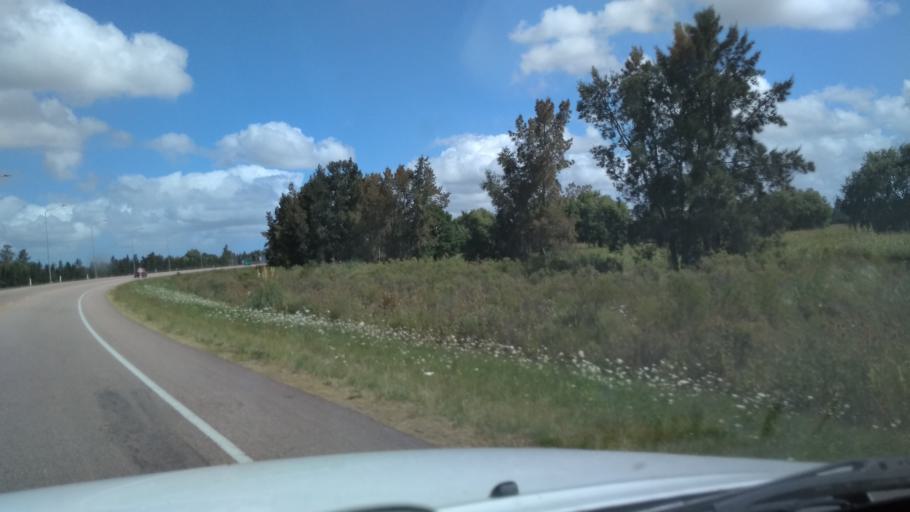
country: UY
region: Canelones
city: Sauce
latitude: -34.6446
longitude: -56.0500
